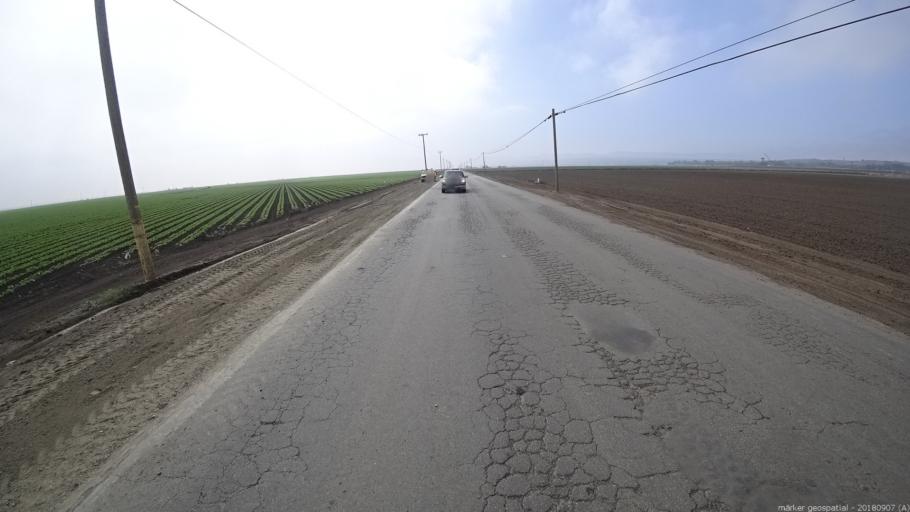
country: US
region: California
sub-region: Monterey County
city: Castroville
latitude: 36.7166
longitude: -121.7412
